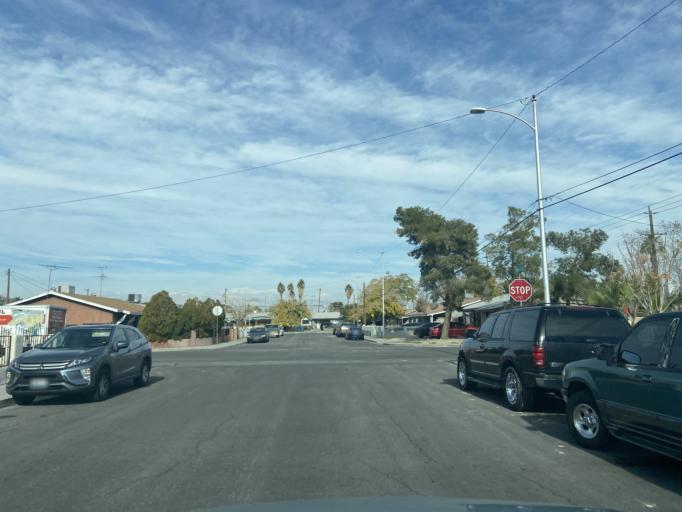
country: US
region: Nevada
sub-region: Clark County
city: North Las Vegas
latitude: 36.1797
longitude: -115.1167
